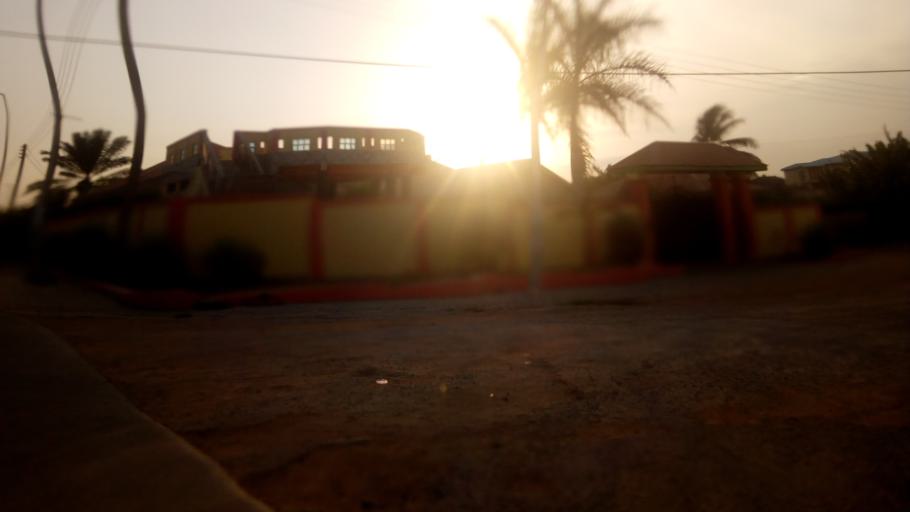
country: GH
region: Central
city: Cape Coast
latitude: 5.1268
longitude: -1.2775
